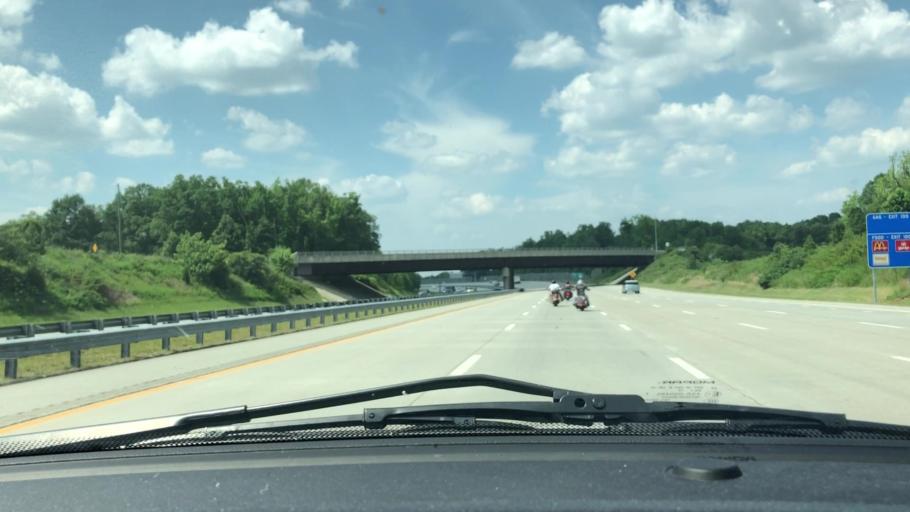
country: US
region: North Carolina
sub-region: Guilford County
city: Jamestown
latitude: 36.0132
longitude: -79.8530
